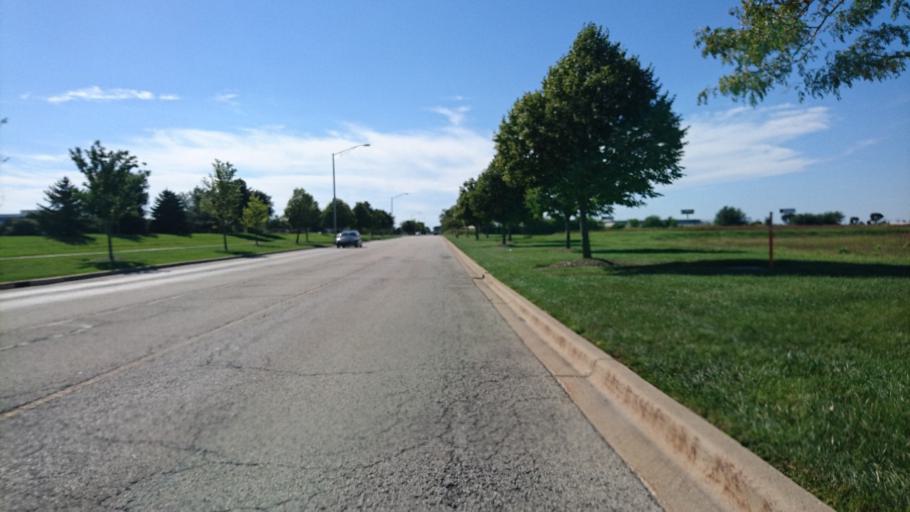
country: US
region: Illinois
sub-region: Will County
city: Ingalls Park
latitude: 41.5114
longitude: -88.0116
